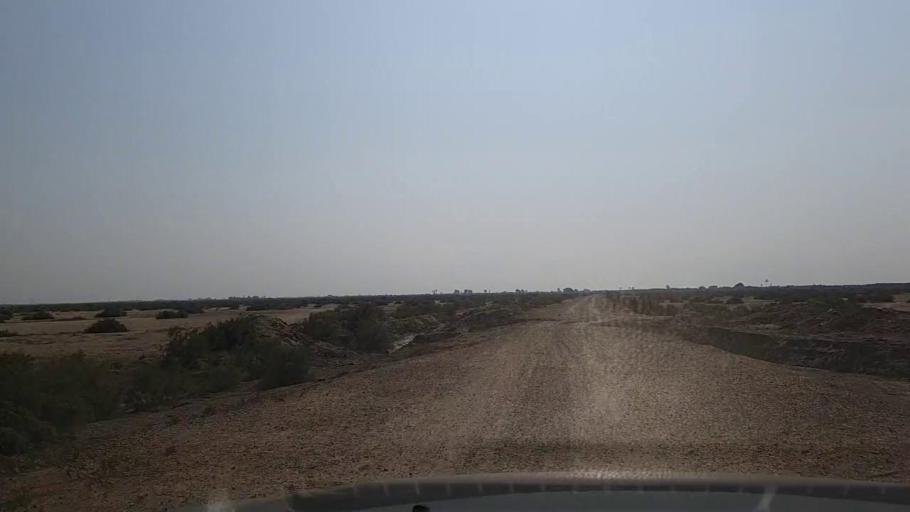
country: PK
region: Sindh
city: Mirpur Sakro
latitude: 24.4303
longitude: 67.7183
